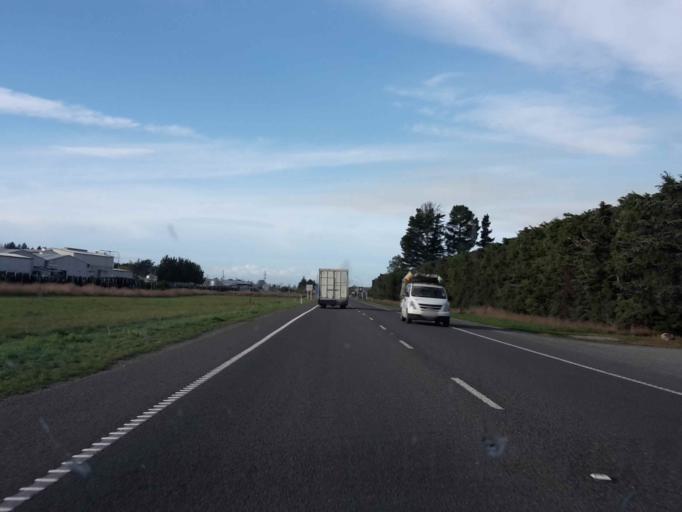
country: NZ
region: Canterbury
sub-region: Ashburton District
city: Tinwald
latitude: -43.9277
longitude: 171.7060
